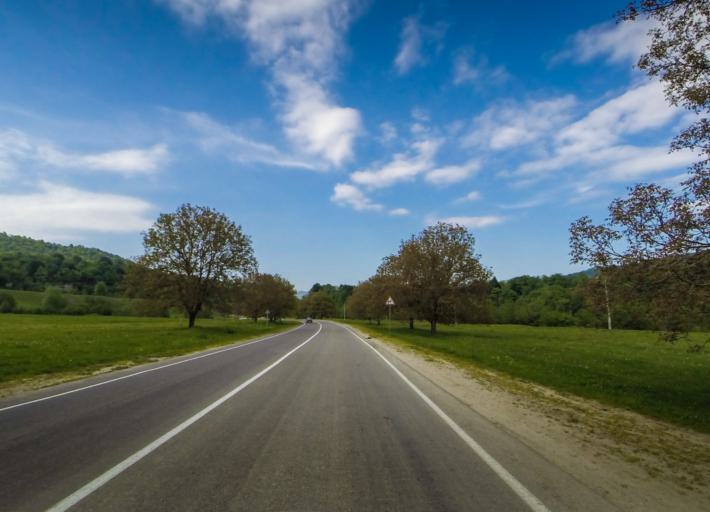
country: RU
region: Kabardino-Balkariya
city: Babugent
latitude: 43.2506
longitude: 43.5342
